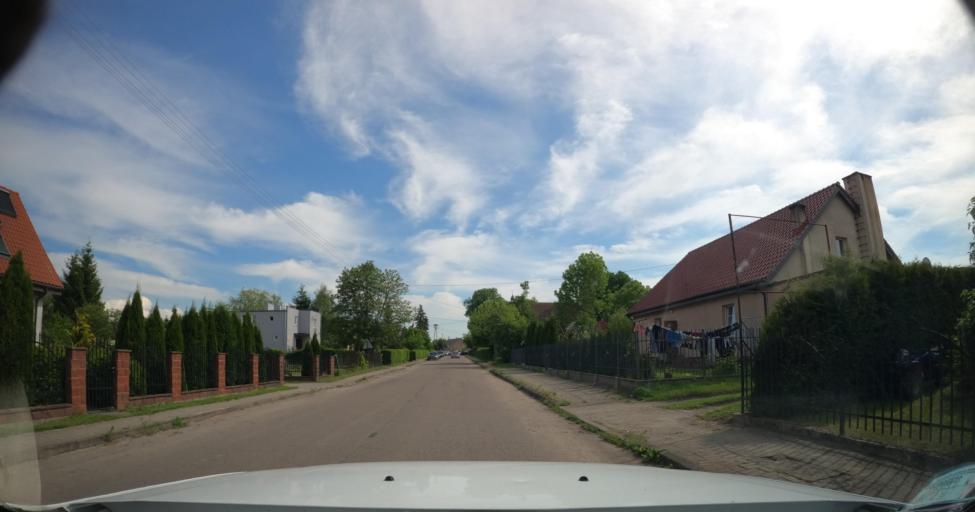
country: PL
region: Warmian-Masurian Voivodeship
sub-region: Powiat lidzbarski
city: Lubomino
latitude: 54.0686
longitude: 20.2391
